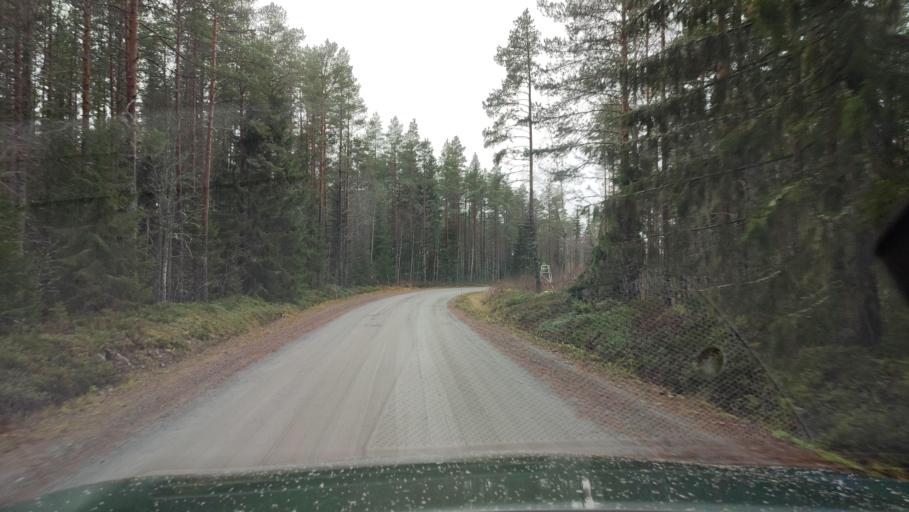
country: FI
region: Ostrobothnia
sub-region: Sydosterbotten
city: Naerpes
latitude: 62.4532
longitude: 21.4734
